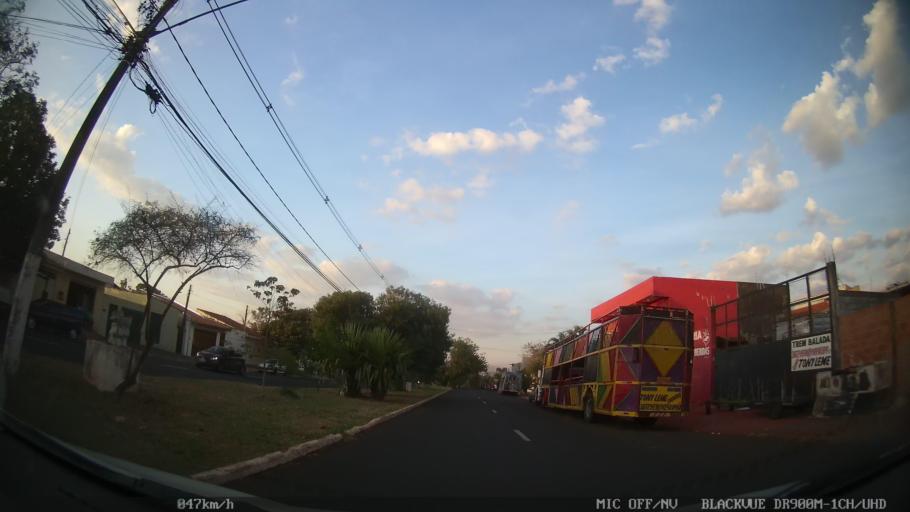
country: BR
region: Sao Paulo
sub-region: Ribeirao Preto
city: Ribeirao Preto
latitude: -21.1349
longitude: -47.8453
